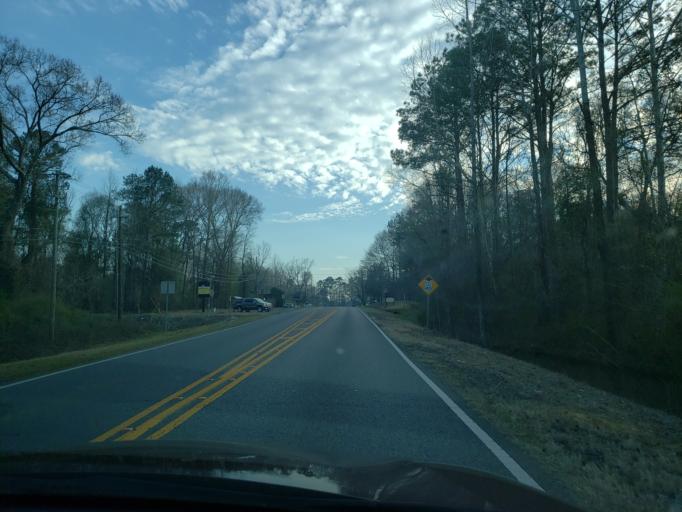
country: US
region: Alabama
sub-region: Hale County
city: Greensboro
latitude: 32.7180
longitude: -87.5943
